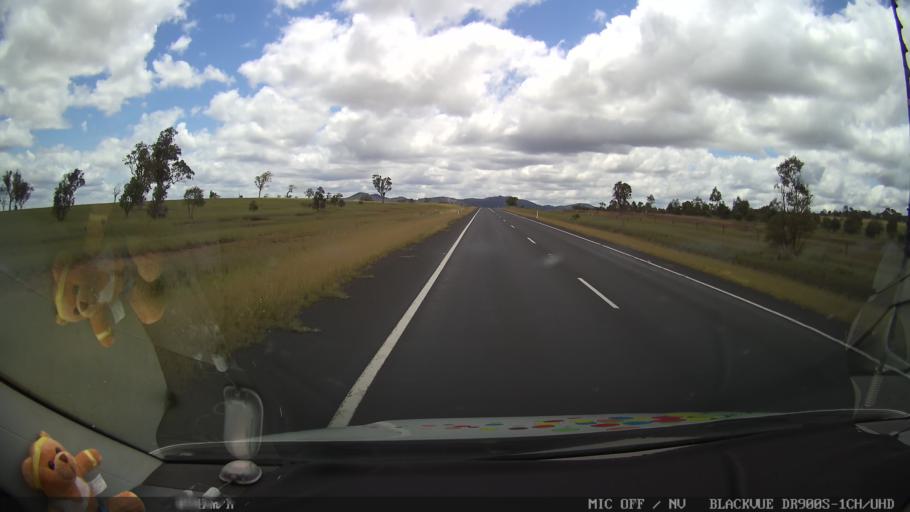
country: AU
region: New South Wales
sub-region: Glen Innes Severn
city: Glen Innes
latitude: -29.3961
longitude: 151.8782
